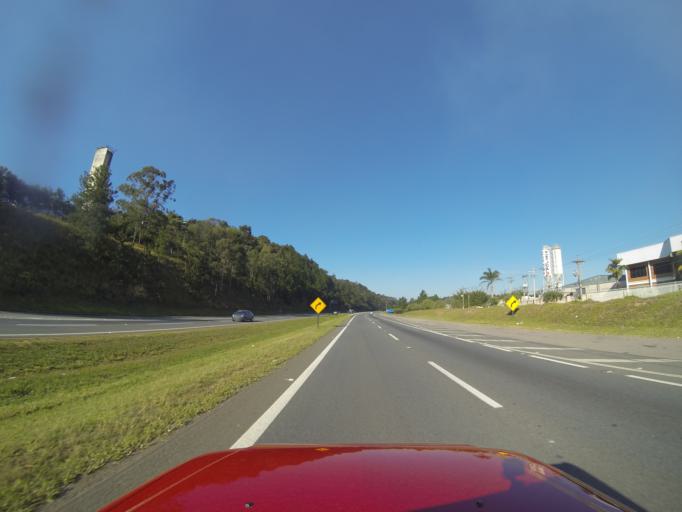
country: BR
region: Sao Paulo
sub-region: Atibaia
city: Atibaia
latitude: -23.1051
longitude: -46.5458
